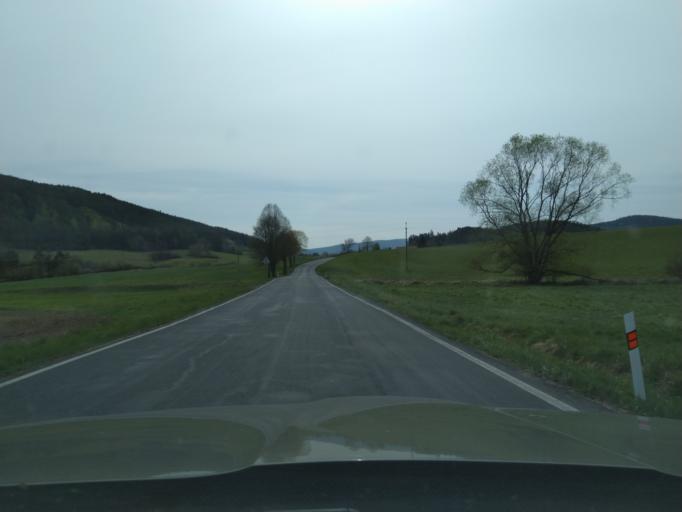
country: CZ
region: Plzensky
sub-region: Okres Klatovy
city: Susice
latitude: 49.2356
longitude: 13.5776
